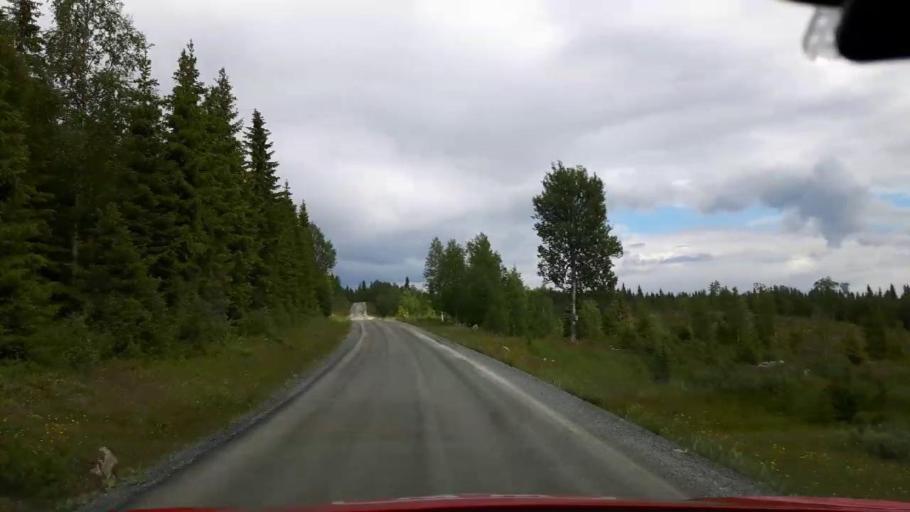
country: NO
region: Nord-Trondelag
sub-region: Lierne
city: Sandvika
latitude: 64.1439
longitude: 13.9314
